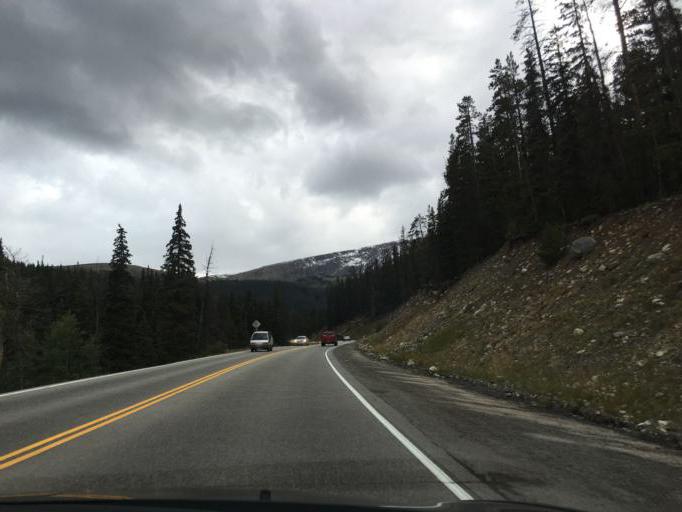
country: US
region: Colorado
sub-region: Summit County
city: Breckenridge
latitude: 39.3851
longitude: -106.0565
